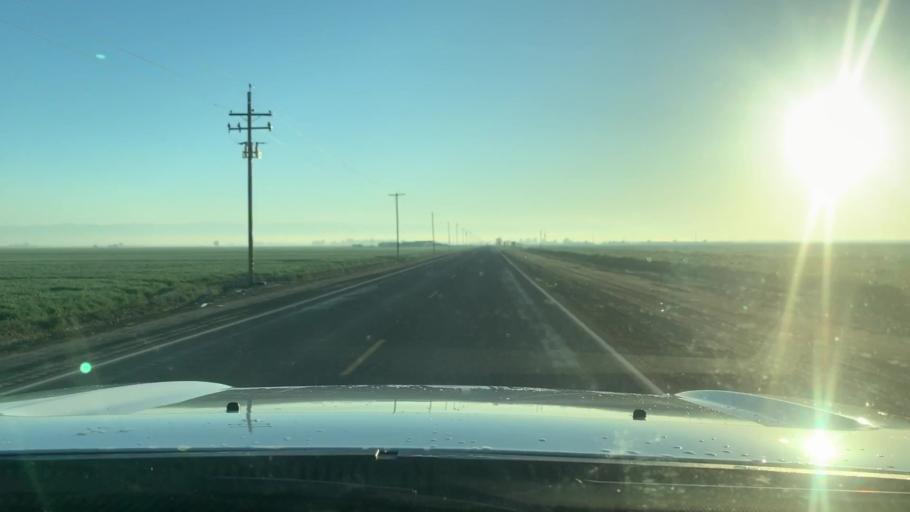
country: US
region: California
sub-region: Kings County
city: Armona
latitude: 36.2111
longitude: -119.6973
